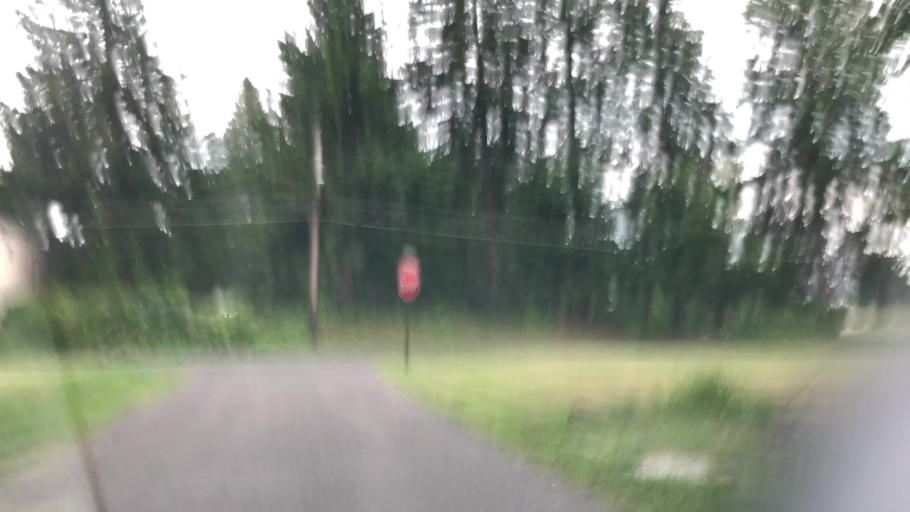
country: US
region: Ohio
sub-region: Stark County
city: North Canton
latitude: 40.8502
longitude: -81.3877
